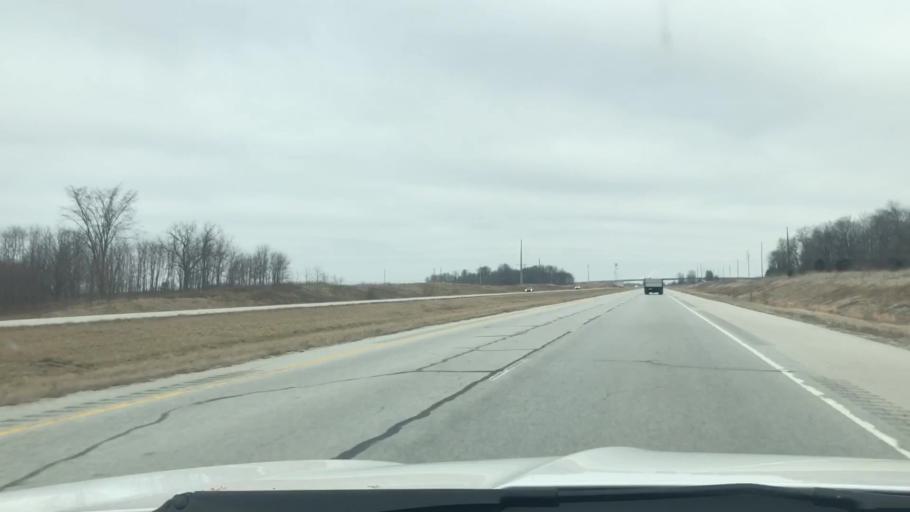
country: US
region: Indiana
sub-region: Cass County
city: Georgetown
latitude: 40.6551
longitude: -86.5495
